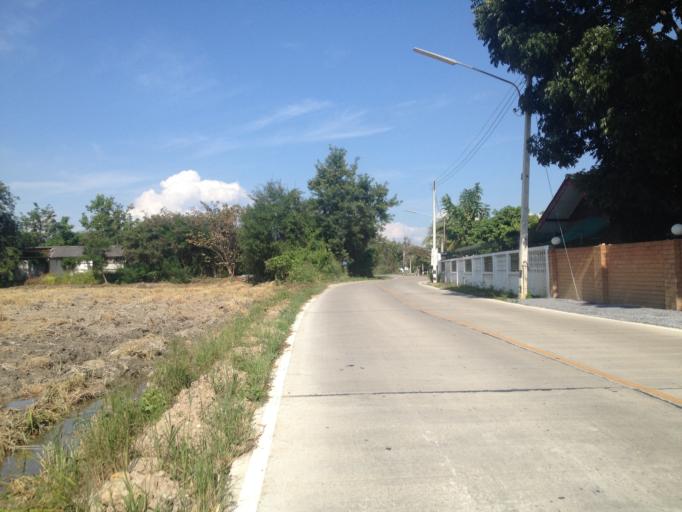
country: TH
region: Chiang Mai
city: Hang Dong
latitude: 18.7176
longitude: 98.9701
